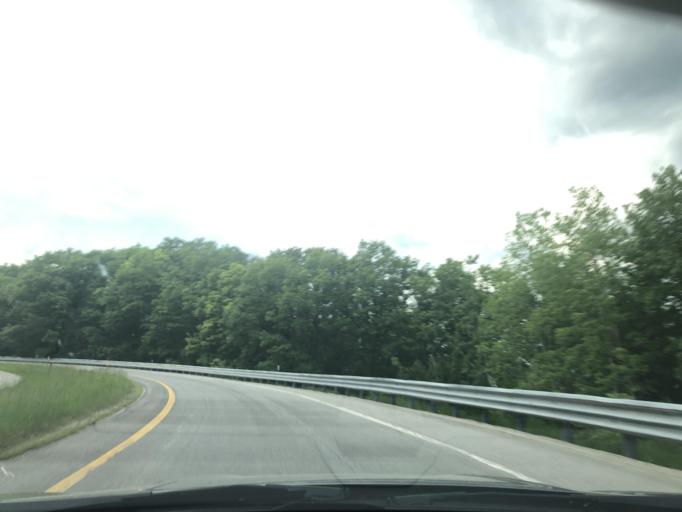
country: US
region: Michigan
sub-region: Clare County
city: Harrison
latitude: 43.9913
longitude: -84.7735
